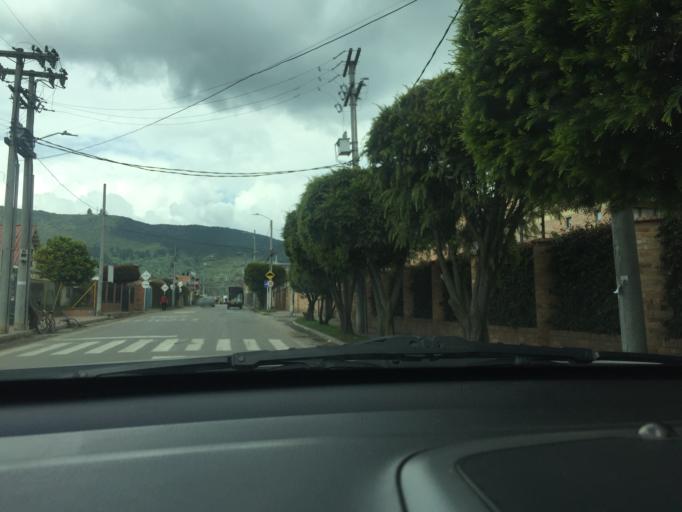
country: CO
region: Cundinamarca
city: Chia
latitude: 4.8733
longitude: -74.0657
